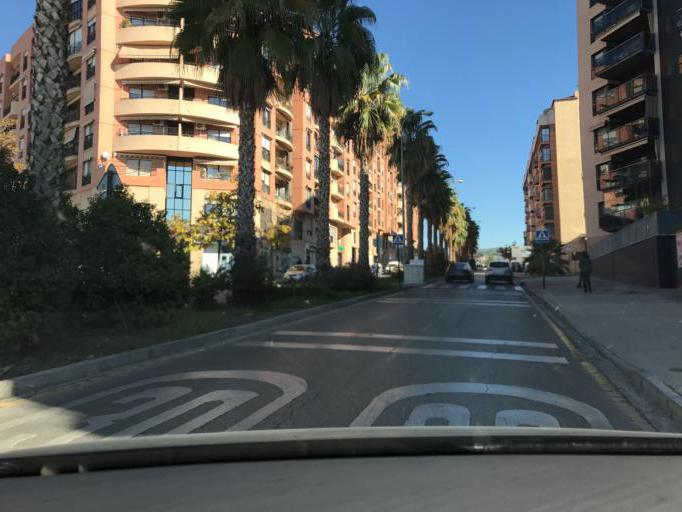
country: ES
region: Andalusia
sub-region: Provincia de Granada
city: Maracena
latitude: 37.1962
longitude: -3.6243
